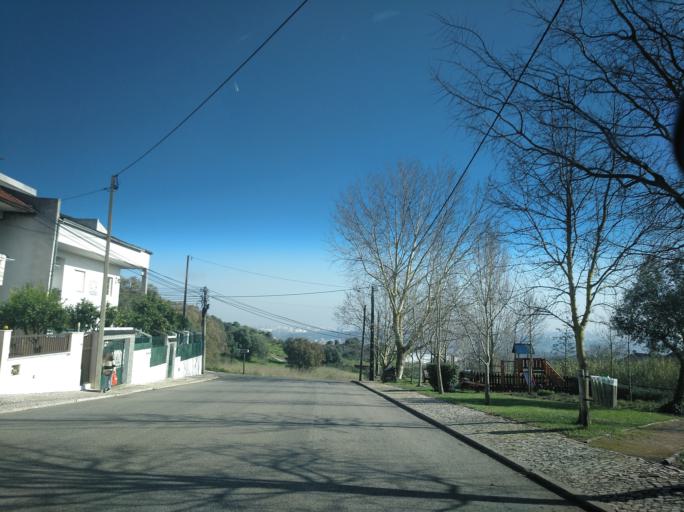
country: PT
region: Lisbon
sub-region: Odivelas
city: Famoes
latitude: 38.7955
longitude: -9.2122
